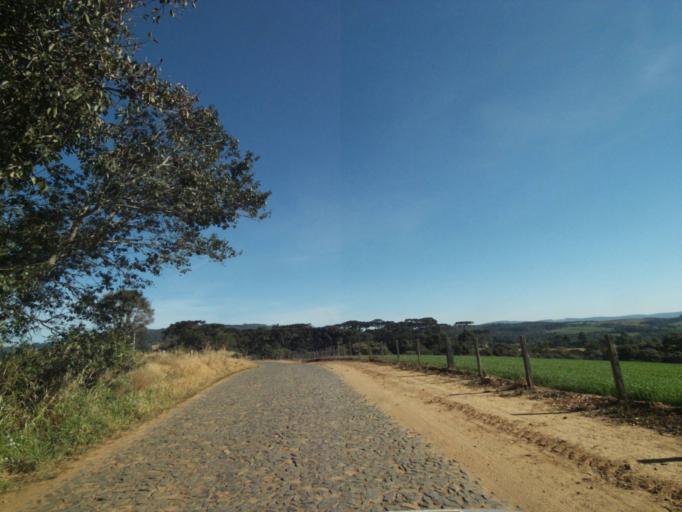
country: BR
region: Parana
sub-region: Tibagi
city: Tibagi
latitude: -24.5284
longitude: -50.4565
